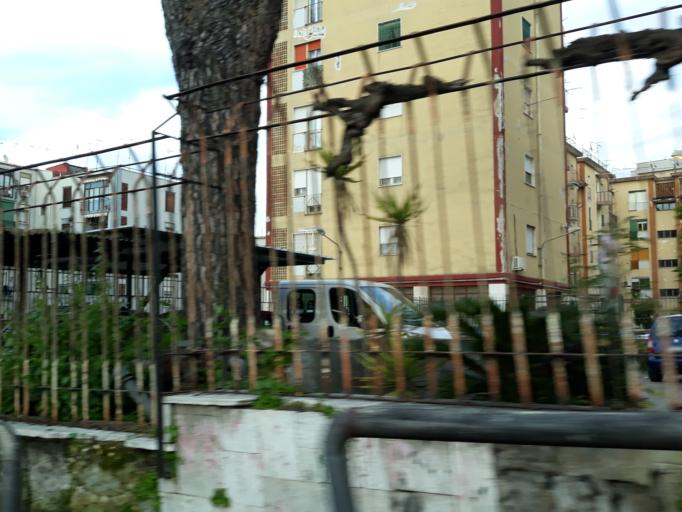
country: IT
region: Campania
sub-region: Provincia di Napoli
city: Mugnano di Napoli
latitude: 40.8914
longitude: 14.2314
